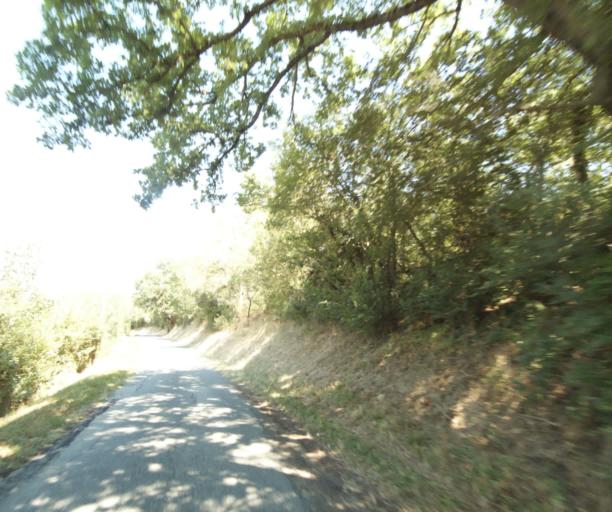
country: FR
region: Midi-Pyrenees
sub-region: Departement de l'Ariege
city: Lezat-sur-Leze
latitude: 43.3032
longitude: 1.3460
